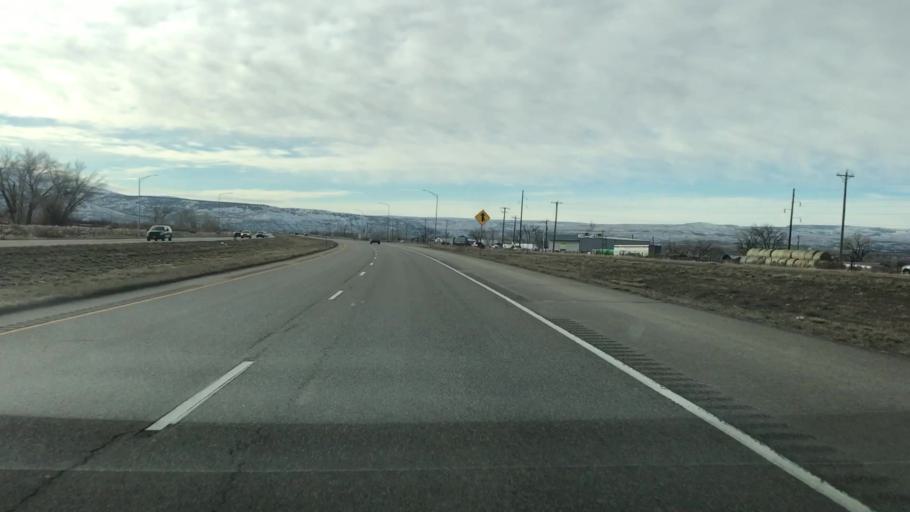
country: US
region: Colorado
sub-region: Garfield County
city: Parachute
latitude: 39.3218
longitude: -108.2095
